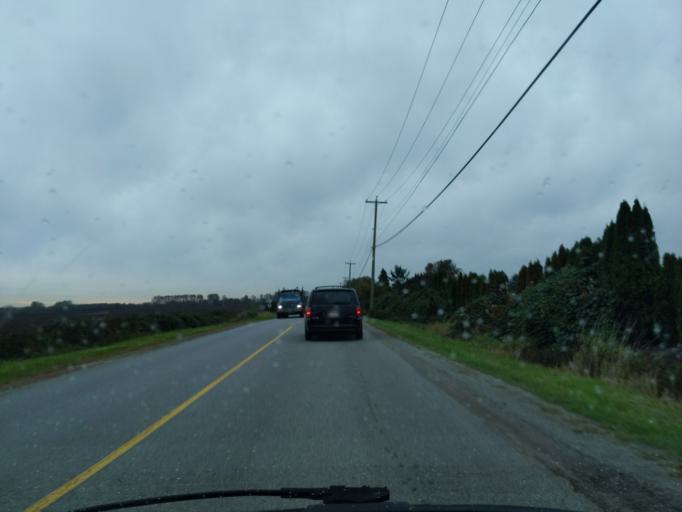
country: CA
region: British Columbia
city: Pitt Meadows
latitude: 49.2222
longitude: -122.7228
